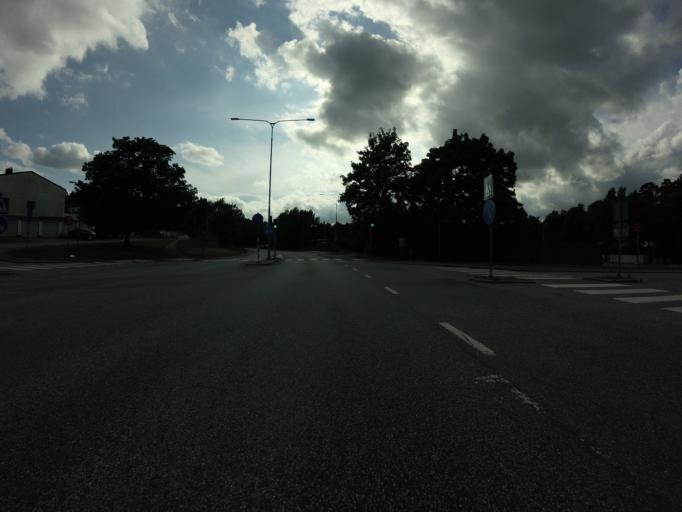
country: SE
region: Stockholm
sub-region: Lidingo
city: Brevik
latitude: 59.3737
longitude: 18.1724
